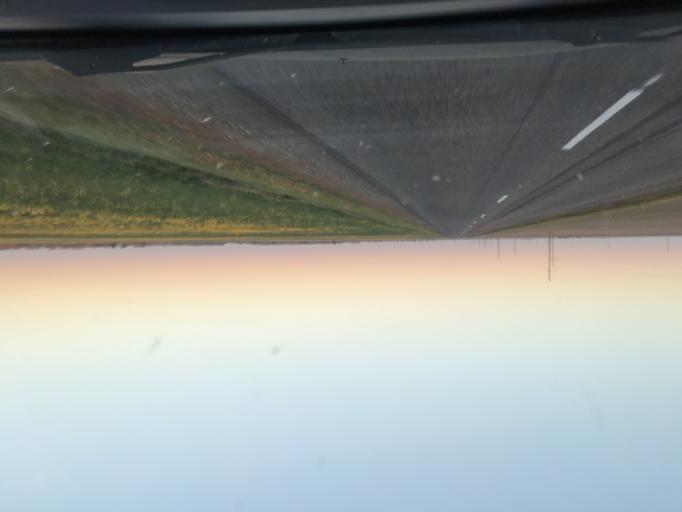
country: BY
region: Gomel
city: Loyew
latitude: 52.1223
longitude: 30.5813
